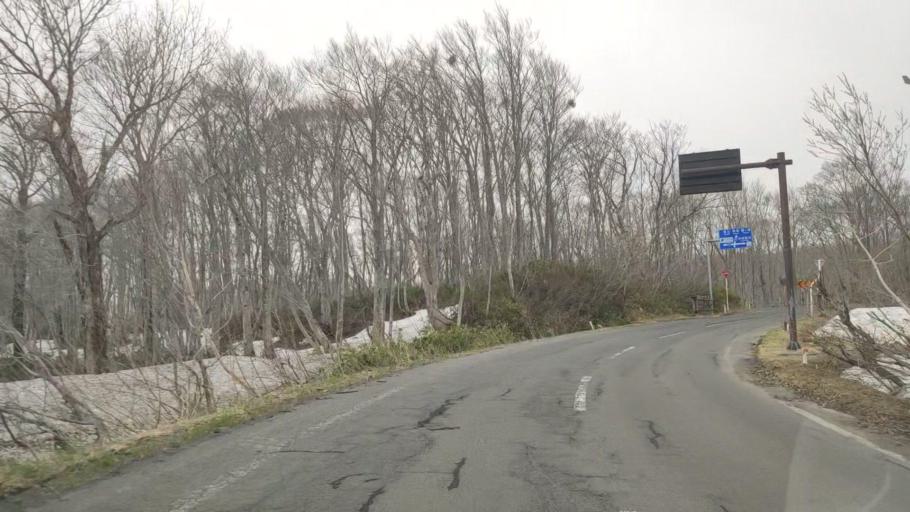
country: JP
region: Aomori
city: Aomori Shi
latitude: 40.6318
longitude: 140.9294
